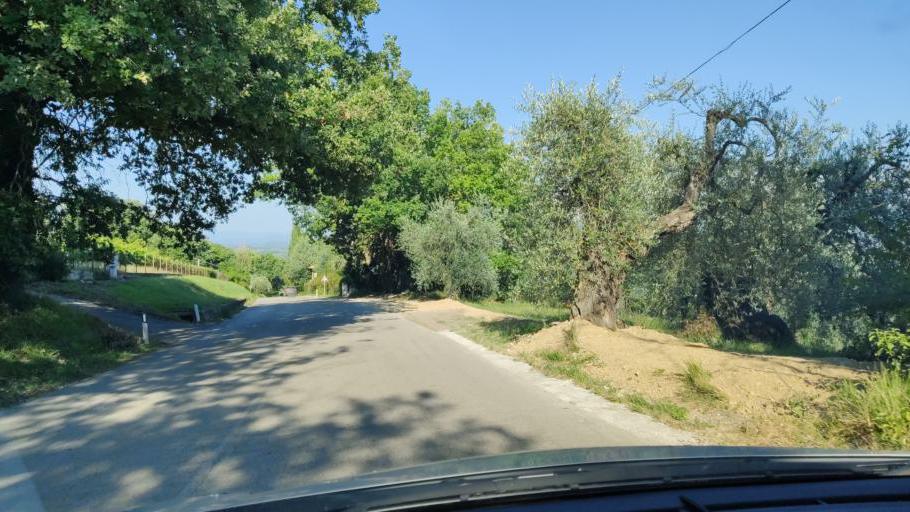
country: IT
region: Umbria
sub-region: Provincia di Terni
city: Penna in Teverina
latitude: 42.4879
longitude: 12.3580
